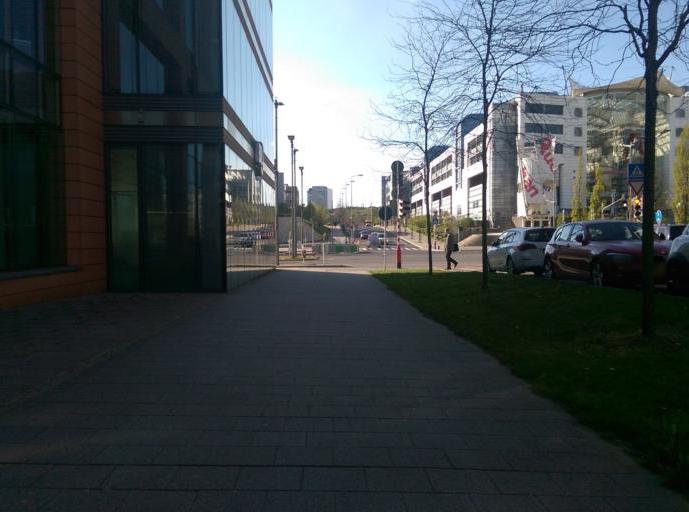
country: LU
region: Luxembourg
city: Kirchberg
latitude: 49.6313
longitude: 6.1711
